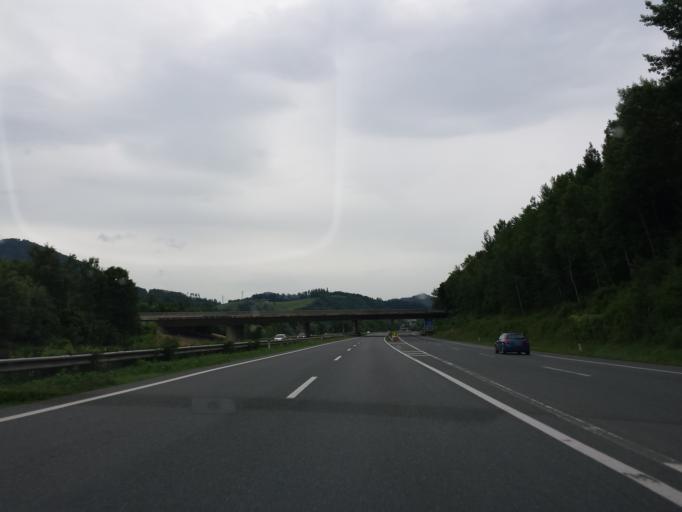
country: AT
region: Styria
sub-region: Politischer Bezirk Graz-Umgebung
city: Deutschfeistritz
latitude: 47.1770
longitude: 15.3315
